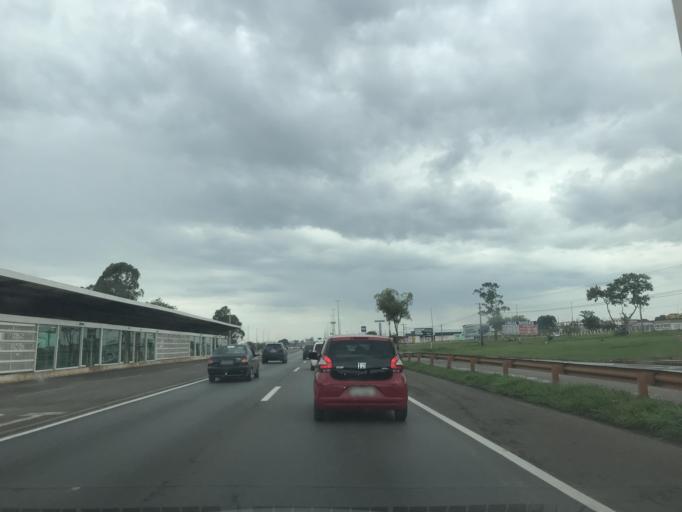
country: BR
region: Federal District
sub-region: Brasilia
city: Brasilia
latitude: -15.9922
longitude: -47.9864
